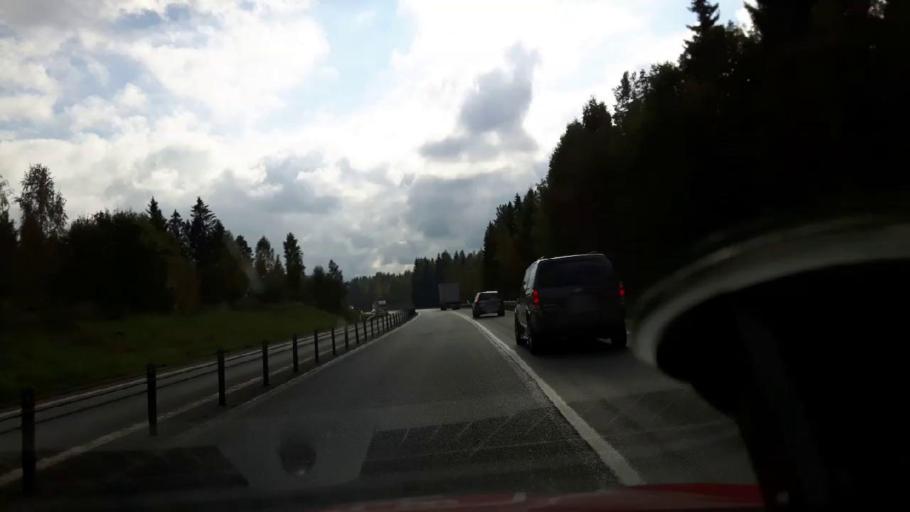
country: SE
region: Gaevleborg
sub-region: Gavle Kommun
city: Norrsundet
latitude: 60.9301
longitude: 17.0103
